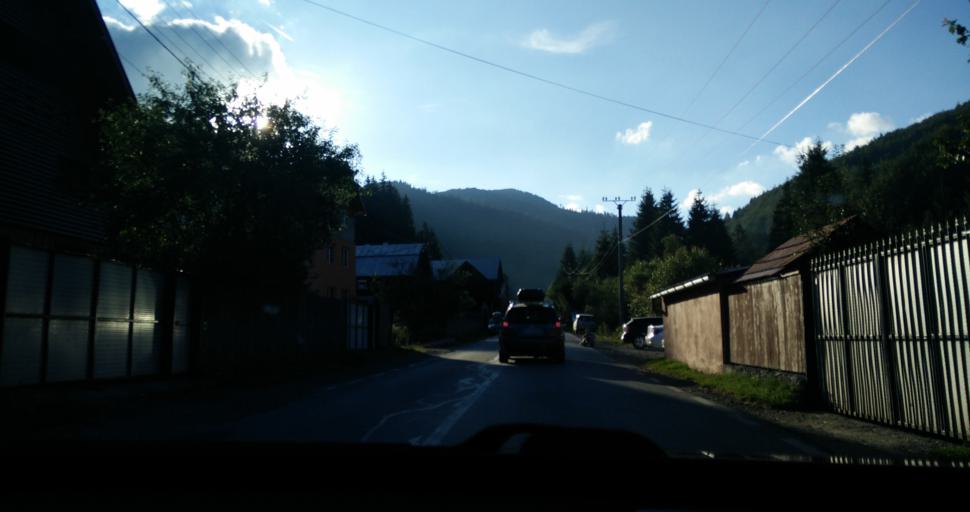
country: RO
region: Alba
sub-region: Comuna Arieseni
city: Arieseni
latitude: 46.4811
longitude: 22.7277
